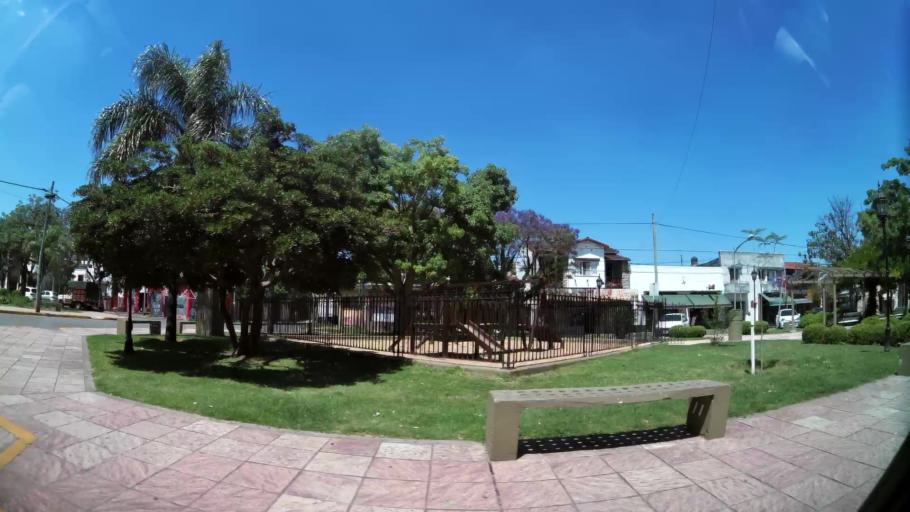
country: AR
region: Buenos Aires
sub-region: Partido de Tigre
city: Tigre
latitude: -34.4319
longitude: -58.5730
